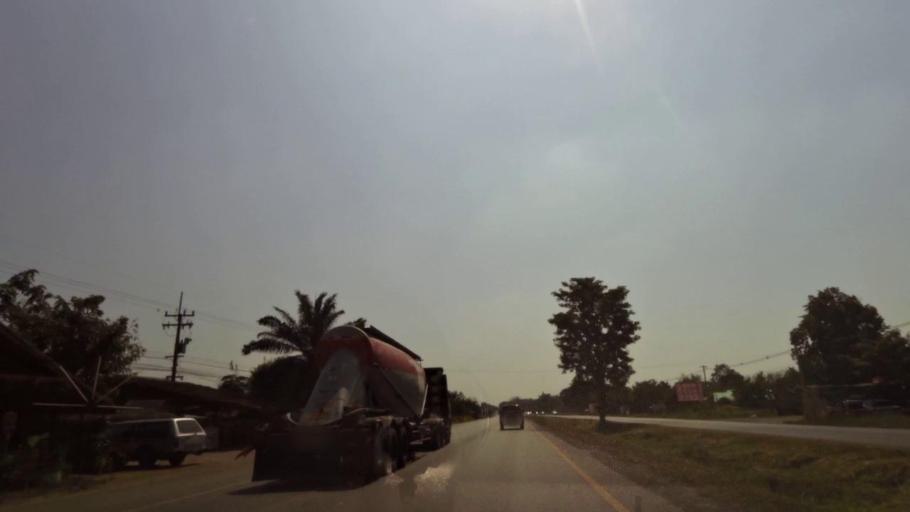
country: TH
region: Phichit
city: Bueng Na Rang
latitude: 16.3451
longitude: 100.1283
